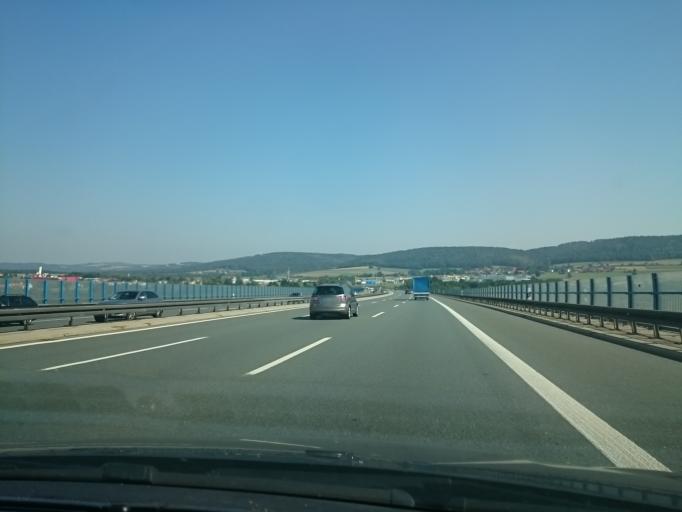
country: DE
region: Bavaria
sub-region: Upper Franconia
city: Himmelkron
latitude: 50.0406
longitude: 11.6129
